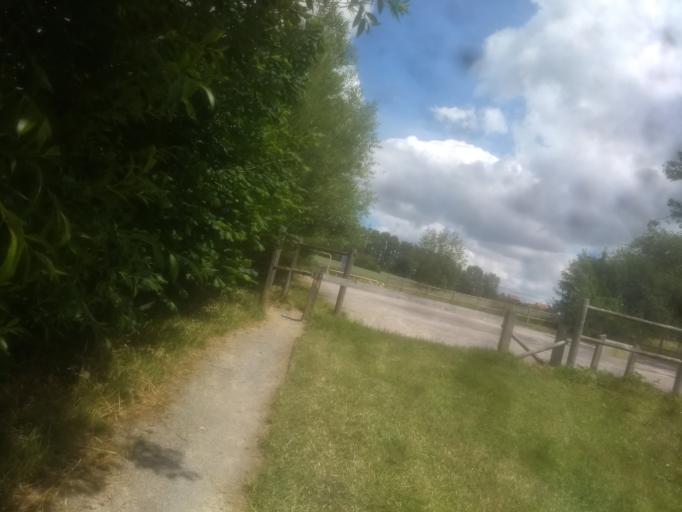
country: FR
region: Nord-Pas-de-Calais
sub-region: Departement du Pas-de-Calais
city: Maroeuil
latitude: 50.3175
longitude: 2.7074
